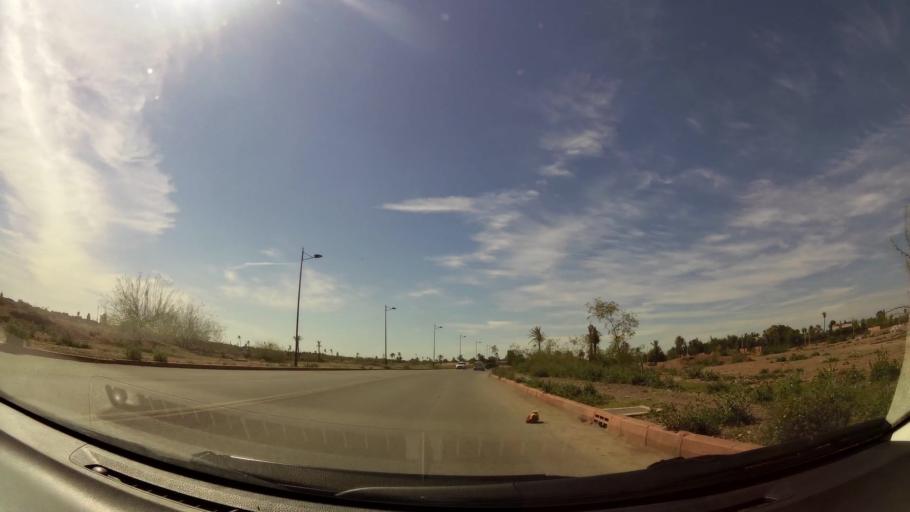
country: MA
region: Marrakech-Tensift-Al Haouz
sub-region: Marrakech
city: Marrakesh
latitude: 31.6175
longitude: -7.9559
